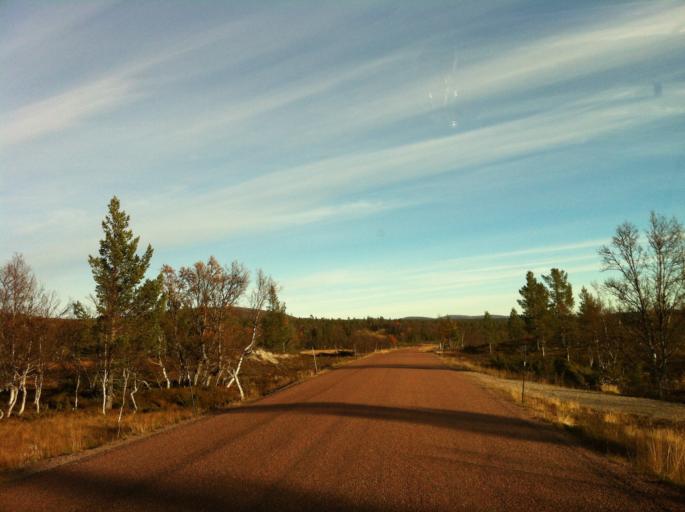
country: NO
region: Hedmark
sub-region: Engerdal
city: Engerdal
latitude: 62.0835
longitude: 12.1097
